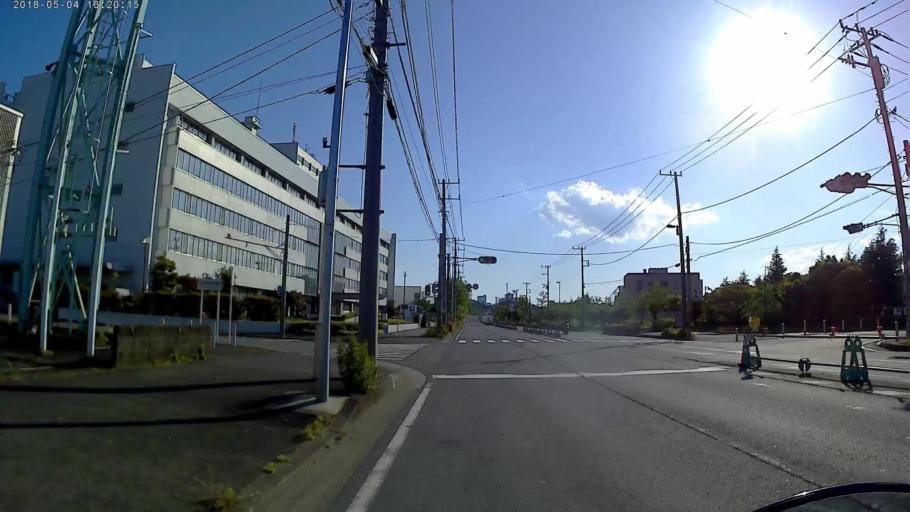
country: JP
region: Kanagawa
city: Yokohama
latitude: 35.4821
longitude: 139.6640
